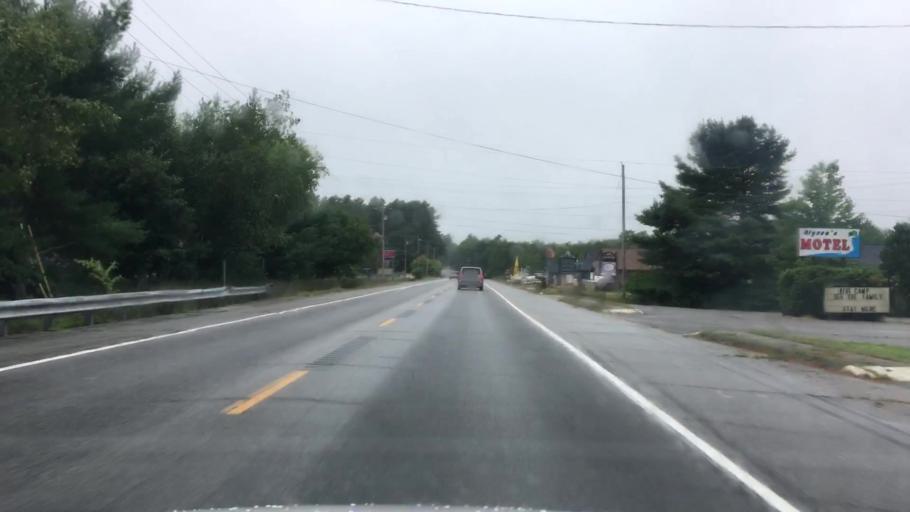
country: US
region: Maine
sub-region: Cumberland County
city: Raymond
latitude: 43.9117
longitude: -70.5098
